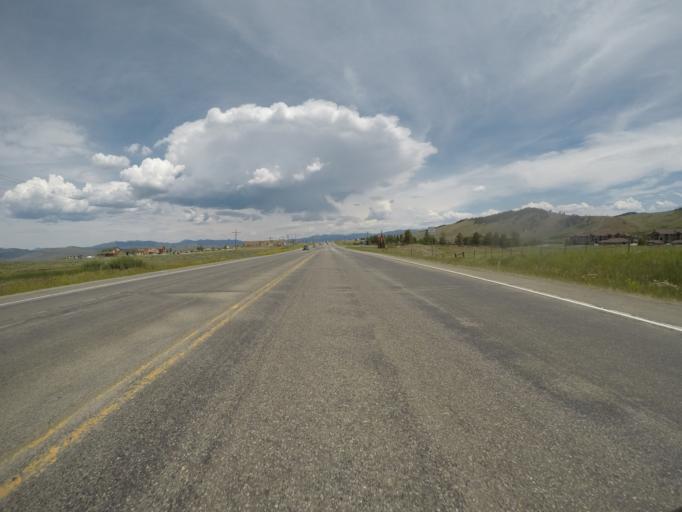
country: US
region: Colorado
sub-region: Grand County
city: Granby
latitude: 40.0592
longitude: -105.9282
